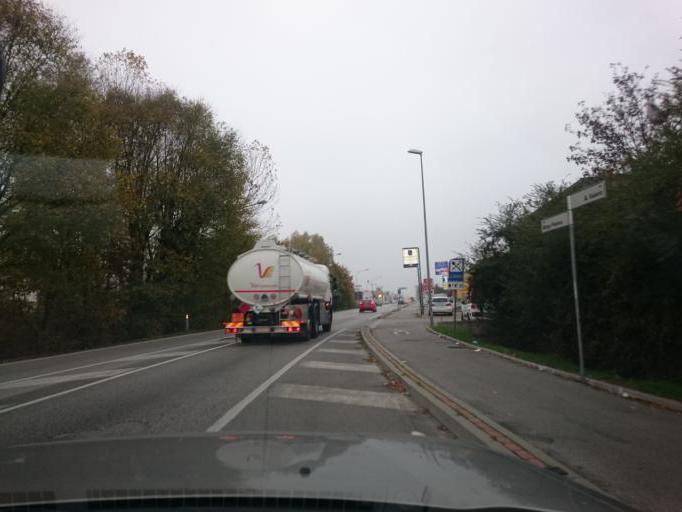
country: IT
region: Veneto
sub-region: Provincia di Padova
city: Piove di Sacco-Piovega
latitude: 45.3018
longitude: 12.0280
